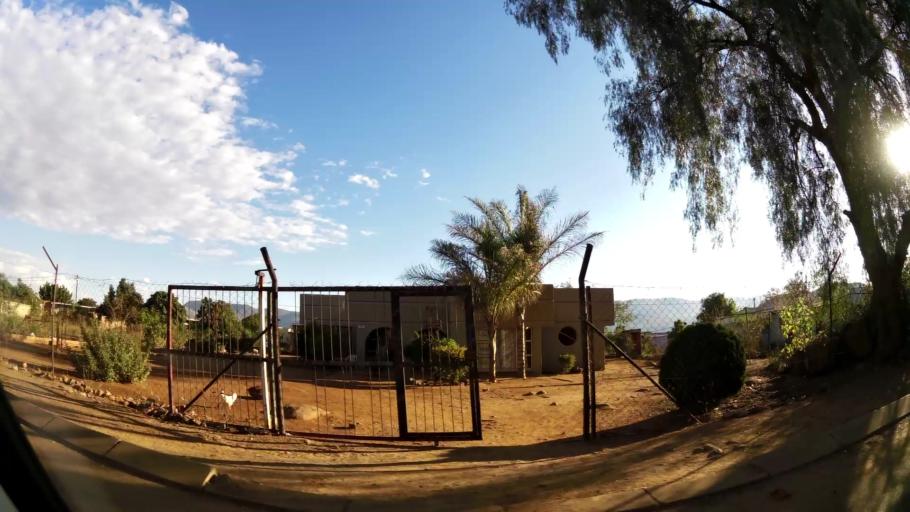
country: ZA
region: Limpopo
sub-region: Waterberg District Municipality
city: Mokopane
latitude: -24.1632
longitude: 28.9888
